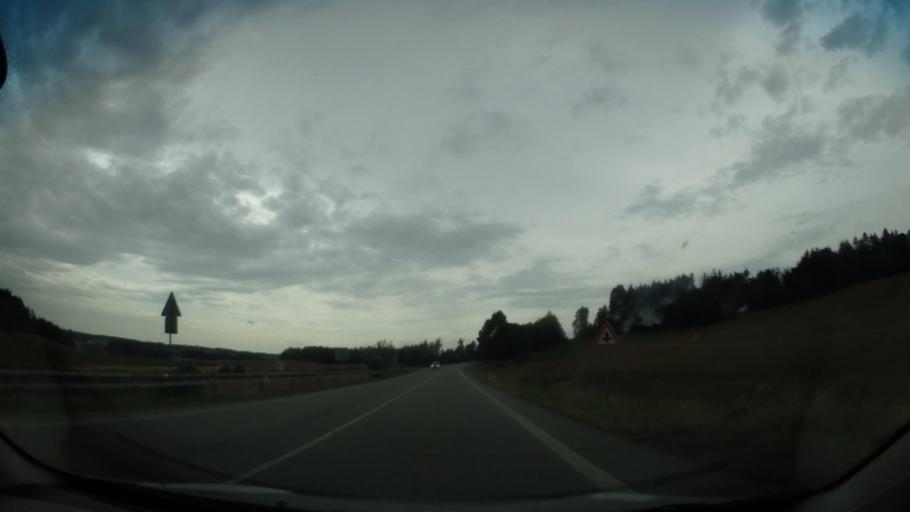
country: CZ
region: Vysocina
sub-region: Okres Zd'ar nad Sazavou
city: Nove Mesto na Morave
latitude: 49.5607
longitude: 16.0509
